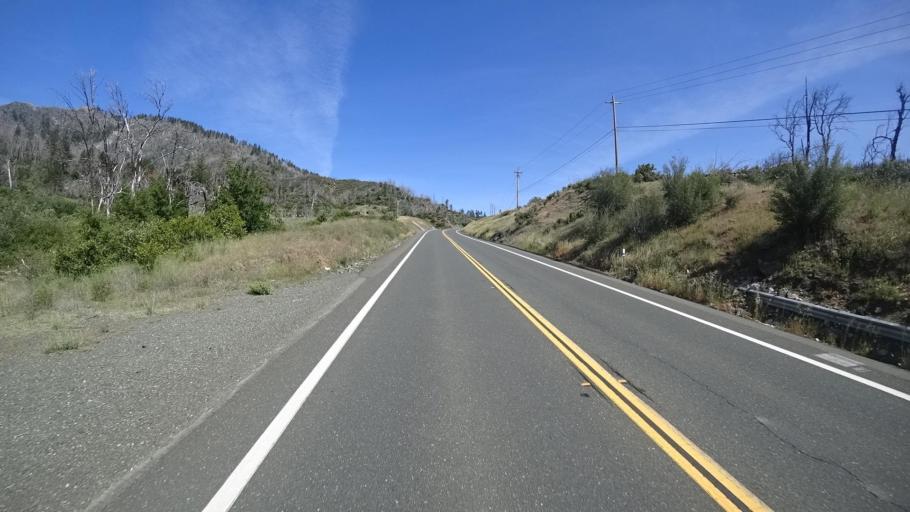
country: US
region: California
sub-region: Lake County
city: Cobb
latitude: 38.7979
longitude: -122.7044
